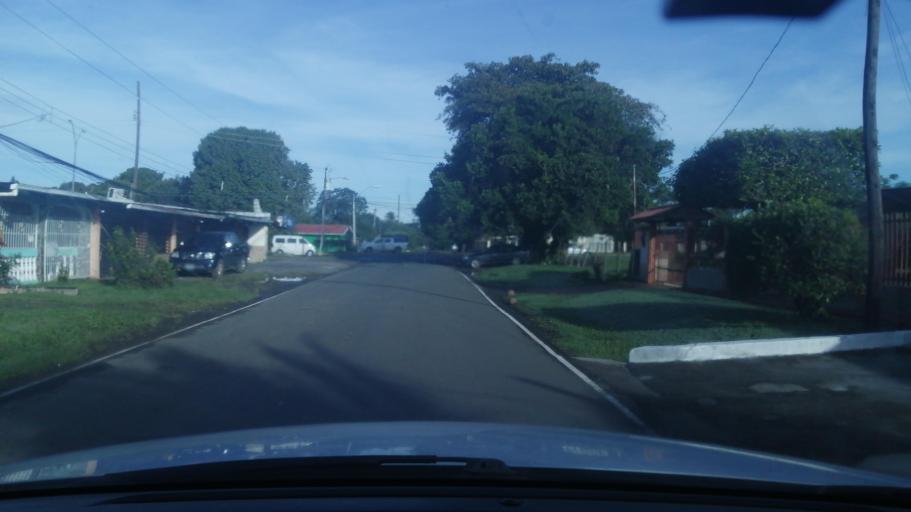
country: PA
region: Chiriqui
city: David
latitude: 8.4486
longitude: -82.4238
